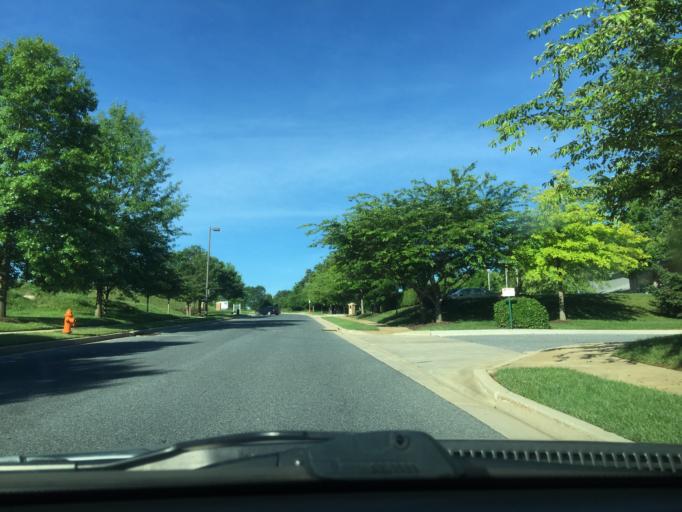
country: US
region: Maryland
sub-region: Baltimore County
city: Hunt Valley
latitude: 39.5133
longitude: -76.6428
